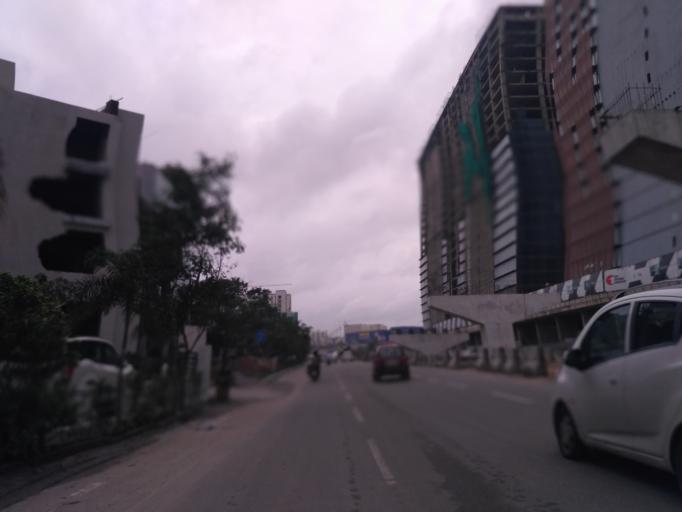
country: IN
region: Telangana
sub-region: Rangareddi
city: Kukatpalli
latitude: 17.4304
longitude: 78.3751
